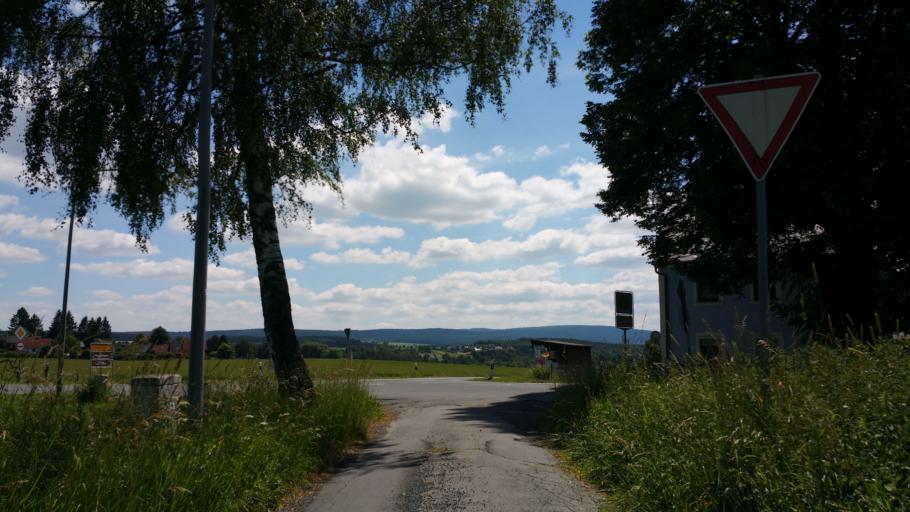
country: DE
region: Bavaria
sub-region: Upper Franconia
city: Schwarzenbach an der Saale
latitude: 50.2219
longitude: 11.9201
